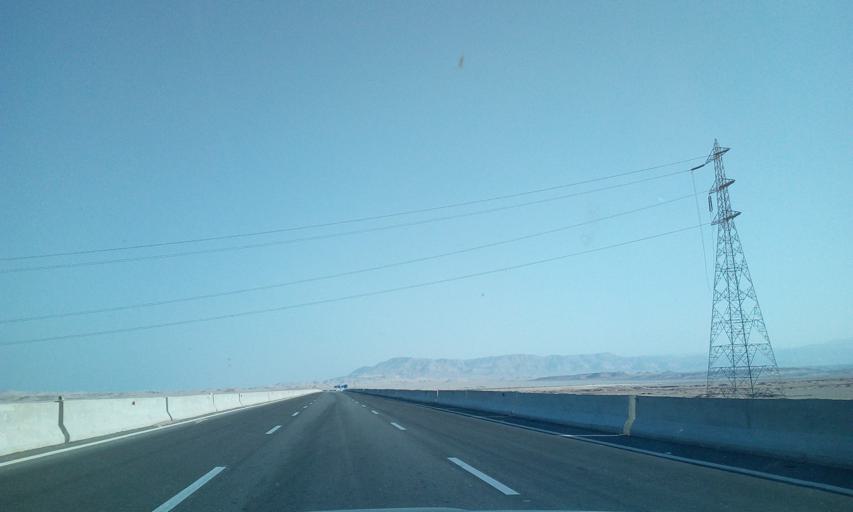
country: EG
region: As Suways
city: Ain Sukhna
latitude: 29.1199
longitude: 32.5286
